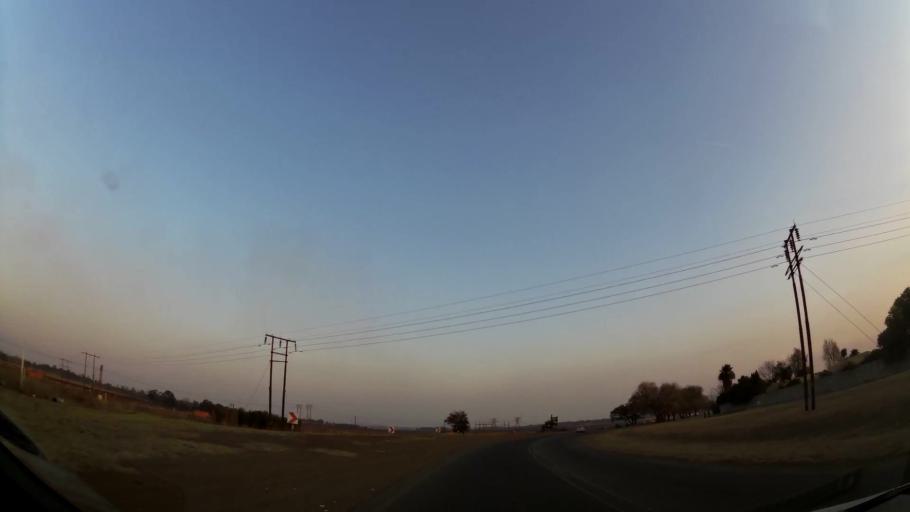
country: ZA
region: Gauteng
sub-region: Ekurhuleni Metropolitan Municipality
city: Springs
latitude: -26.3231
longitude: 28.4493
